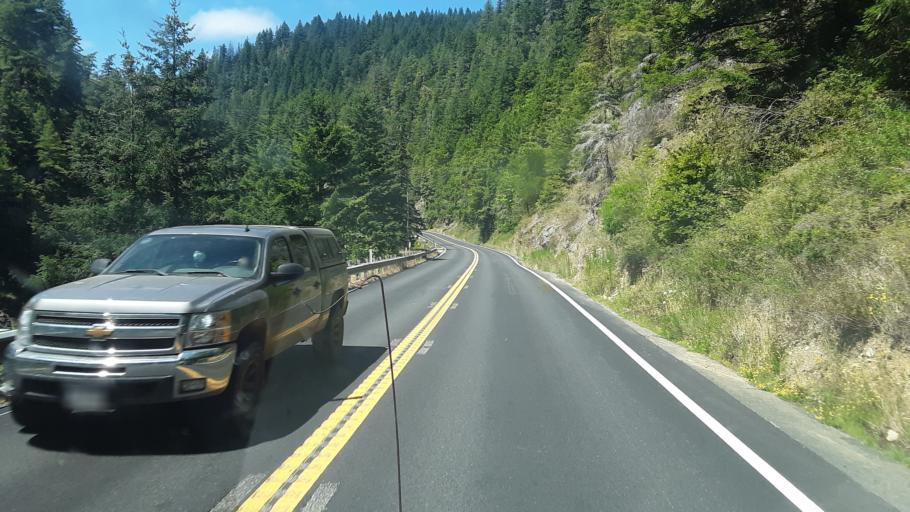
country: US
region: California
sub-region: Del Norte County
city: Bertsch-Oceanview
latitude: 41.8160
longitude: -124.0405
